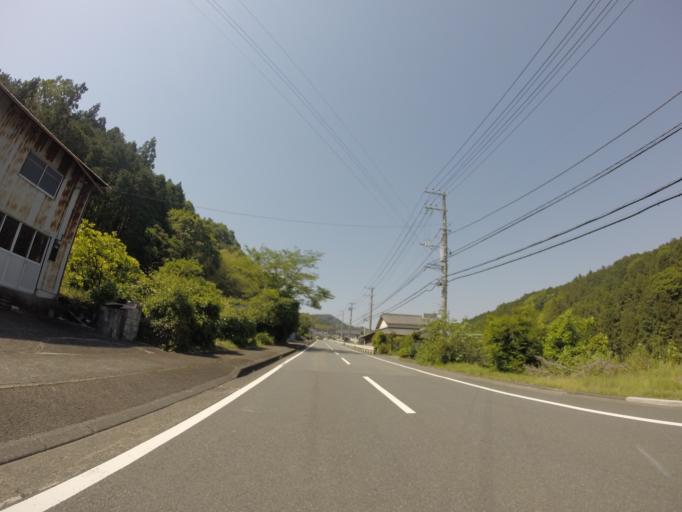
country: JP
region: Shizuoka
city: Fujinomiya
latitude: 35.2060
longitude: 138.5870
